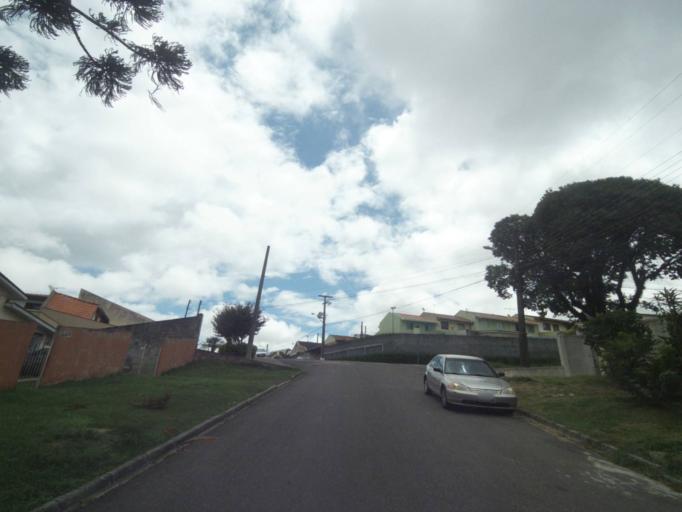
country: BR
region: Parana
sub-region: Curitiba
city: Curitiba
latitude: -25.4843
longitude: -49.2813
